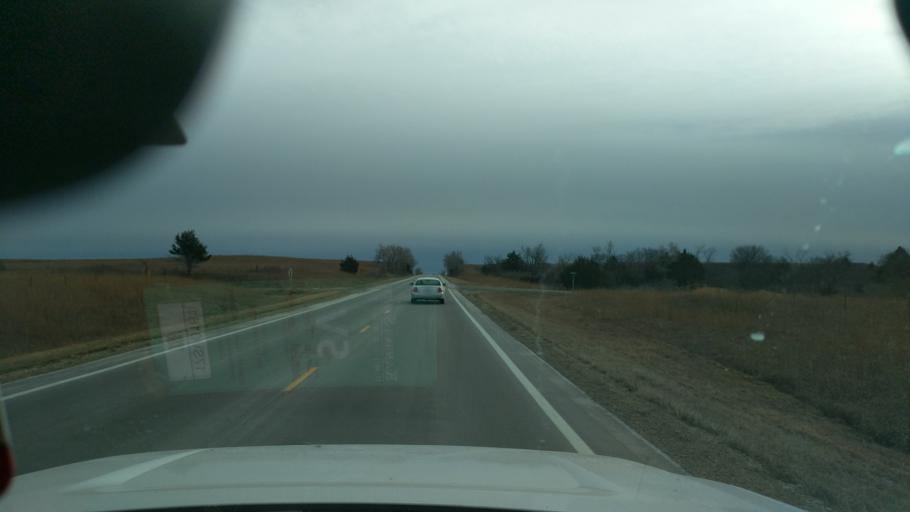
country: US
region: Kansas
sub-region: Geary County
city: Junction City
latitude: 38.9070
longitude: -96.8532
